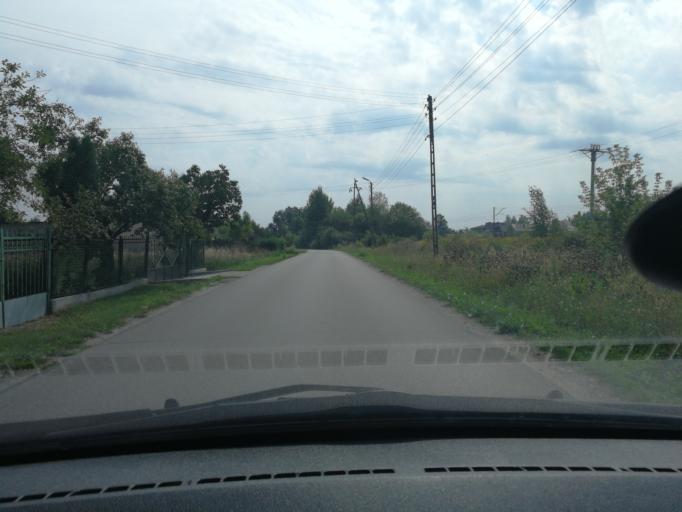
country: PL
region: Lodz Voivodeship
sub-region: Skierniewice
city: Skierniewice
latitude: 51.9727
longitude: 20.1124
